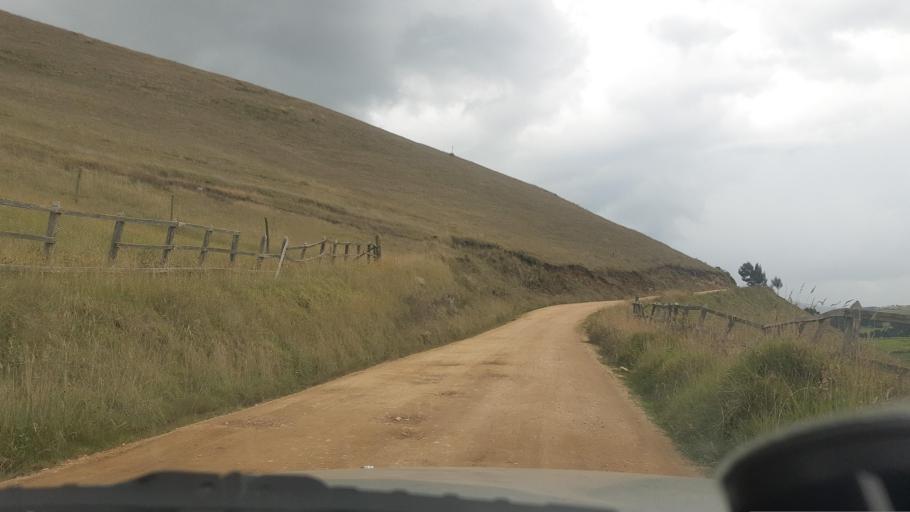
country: CO
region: Cundinamarca
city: Suesca
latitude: 5.1609
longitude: -73.8016
